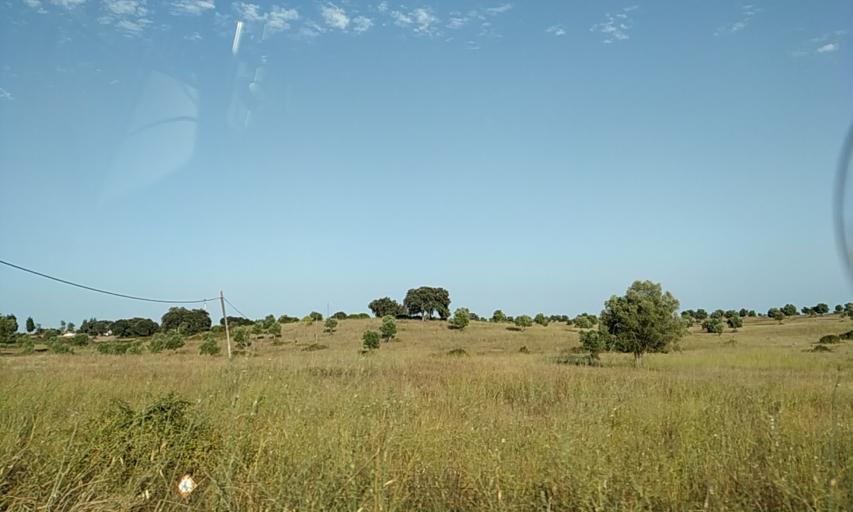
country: PT
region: Santarem
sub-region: Alcanena
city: Alcanena
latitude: 39.3935
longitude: -8.6470
